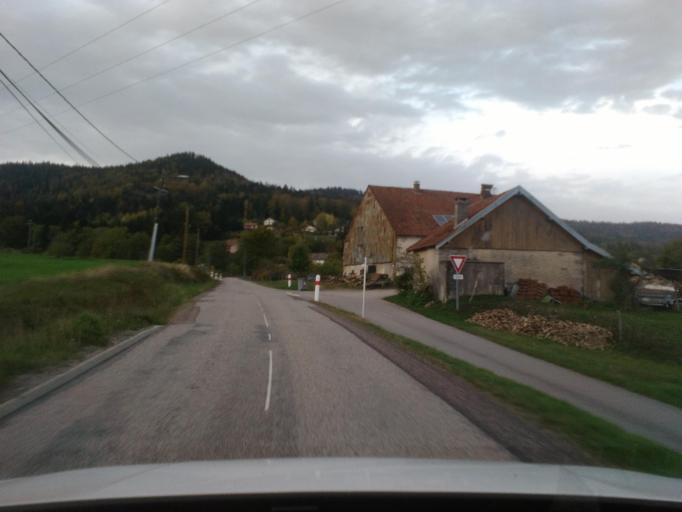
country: FR
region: Lorraine
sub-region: Departement des Vosges
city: Saint-Ame
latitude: 48.0393
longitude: 6.6727
